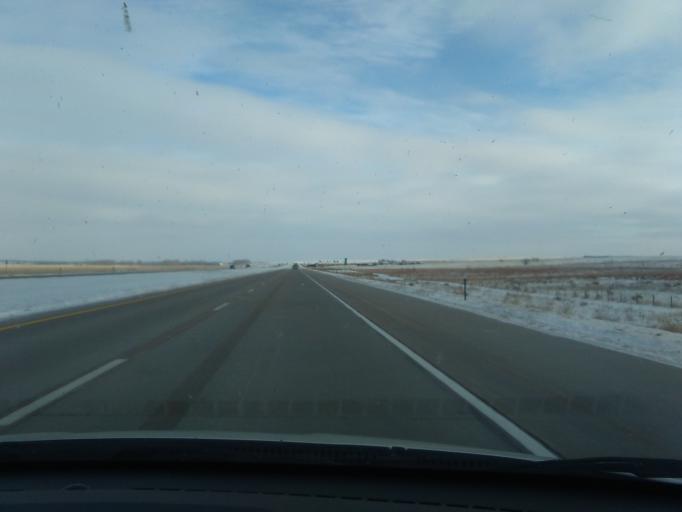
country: US
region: Nebraska
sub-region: Deuel County
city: Chappell
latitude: 41.1058
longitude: -102.5485
